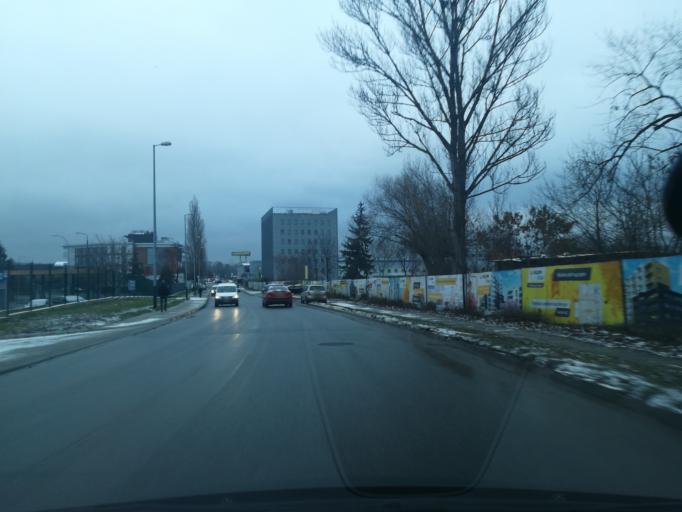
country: PL
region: Lesser Poland Voivodeship
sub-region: Krakow
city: Krakow
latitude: 50.0247
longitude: 19.9604
